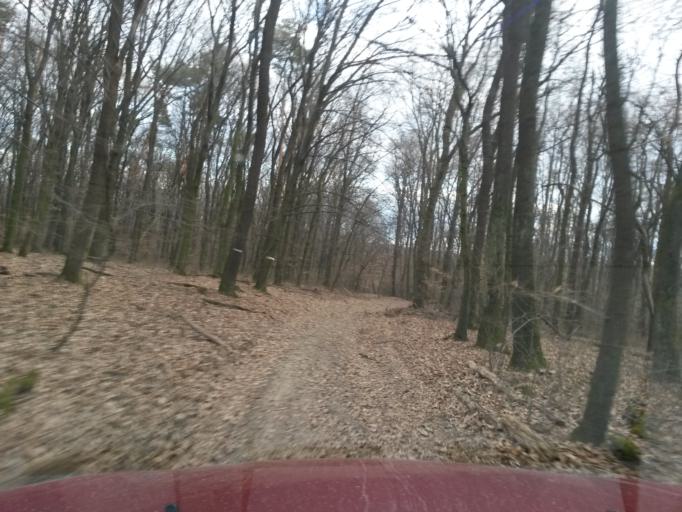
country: SK
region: Kosicky
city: Kosice
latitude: 48.6974
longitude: 21.2980
